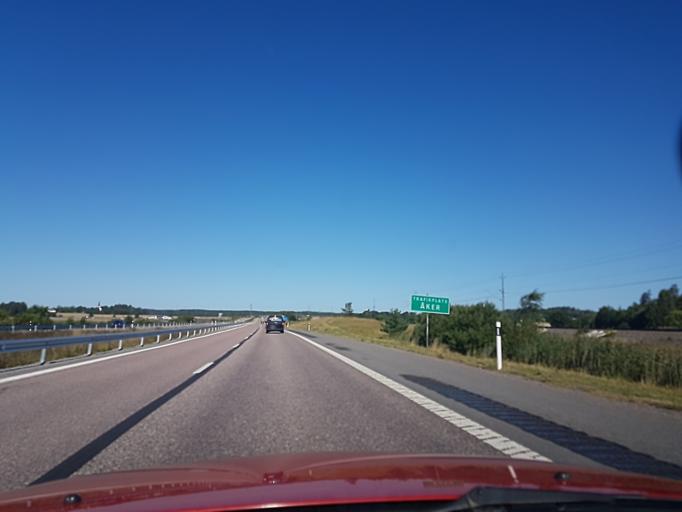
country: SE
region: Soedermanland
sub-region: Strangnas Kommun
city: Akers Styckebruk
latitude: 59.2714
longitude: 17.1310
